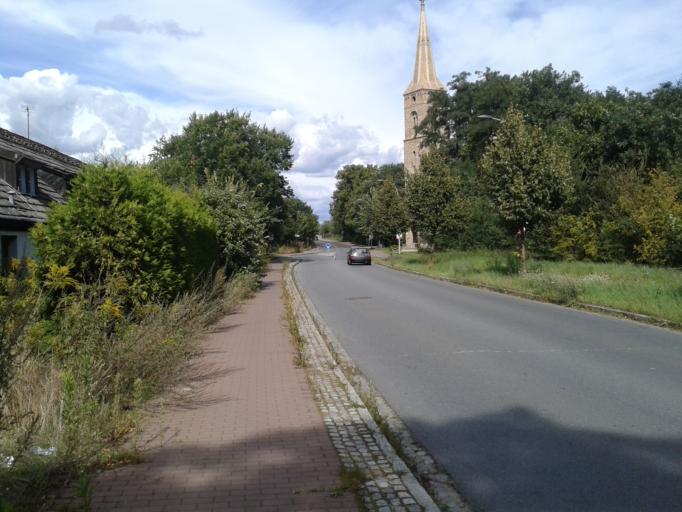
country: DE
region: Brandenburg
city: Hohen Neuendorf
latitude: 52.7033
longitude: 13.2467
